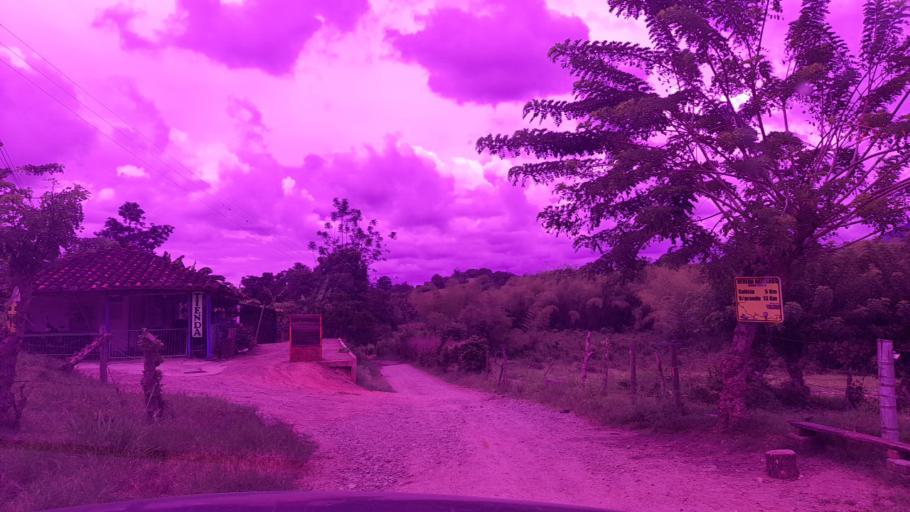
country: CO
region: Valle del Cauca
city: Andalucia
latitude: 4.1657
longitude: -76.0905
